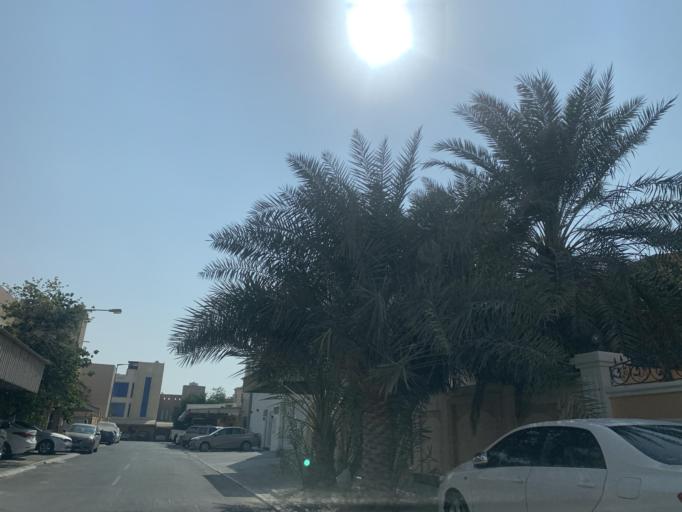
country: BH
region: Central Governorate
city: Madinat Hamad
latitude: 26.1272
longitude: 50.4922
